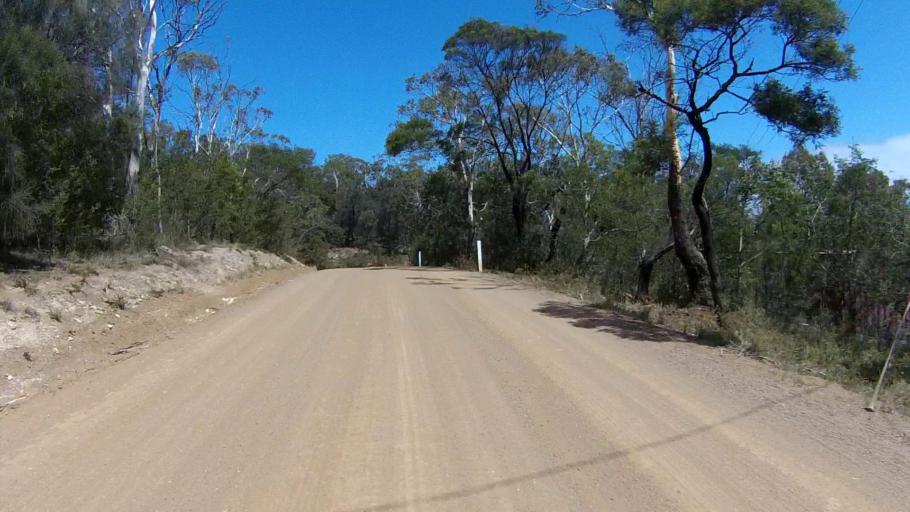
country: AU
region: Tasmania
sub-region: Clarence
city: Lauderdale
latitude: -42.9345
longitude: 147.4633
